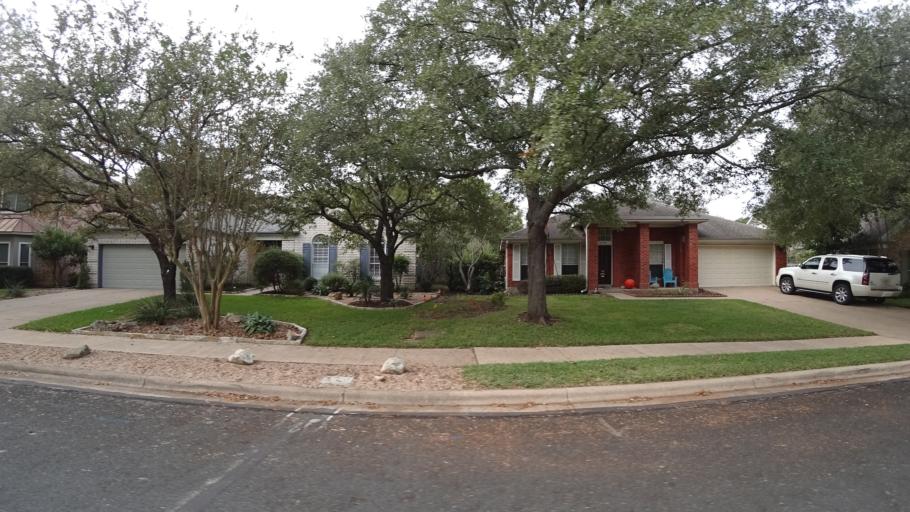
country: US
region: Texas
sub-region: Travis County
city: Shady Hollow
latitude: 30.1919
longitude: -97.8919
